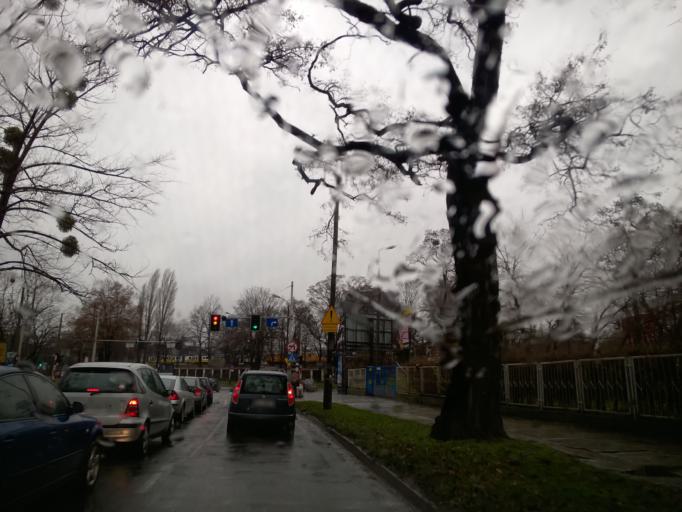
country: PL
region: Lower Silesian Voivodeship
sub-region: Powiat wroclawski
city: Wroclaw
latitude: 51.0961
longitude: 17.0418
